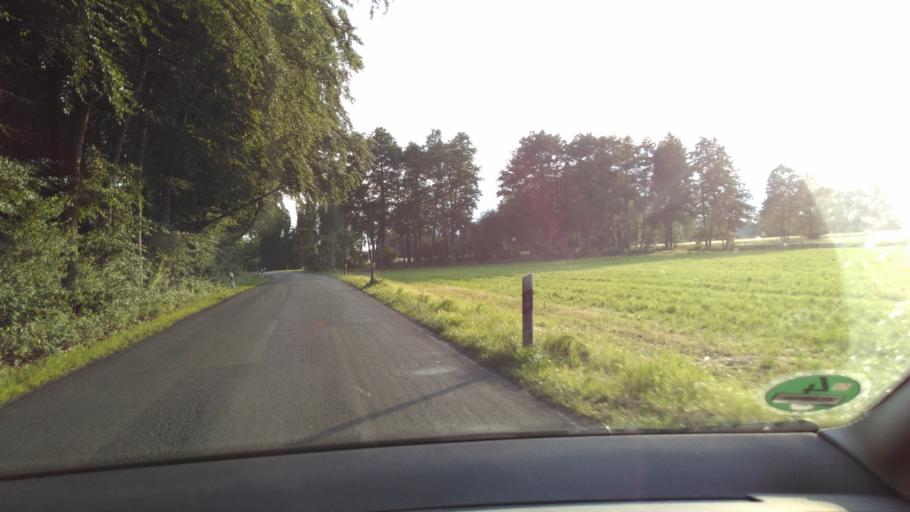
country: DE
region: North Rhine-Westphalia
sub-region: Regierungsbezirk Detmold
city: Verl
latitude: 51.8593
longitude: 8.5115
